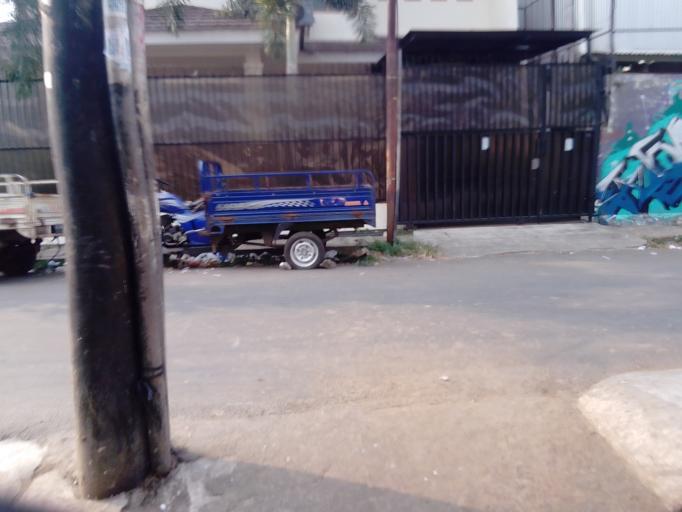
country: ID
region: Jakarta Raya
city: Jakarta
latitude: -6.1966
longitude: 106.8132
